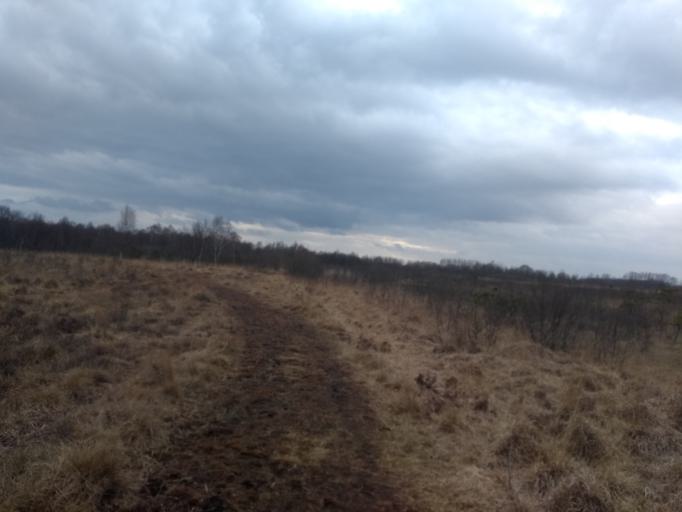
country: NL
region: Overijssel
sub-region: Gemeente Haaksbergen
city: Haaksbergen
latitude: 52.1204
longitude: 6.7805
